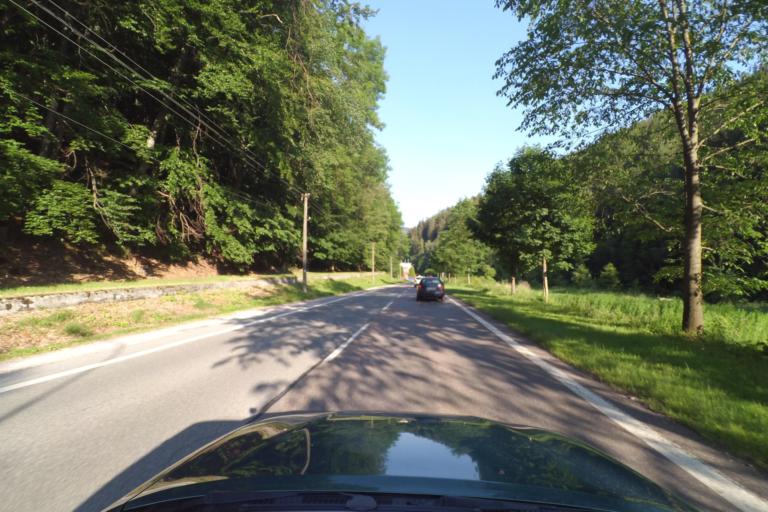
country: CZ
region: Kralovehradecky
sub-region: Okres Trutnov
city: Svoboda nad Upou
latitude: 50.6640
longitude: 15.8089
